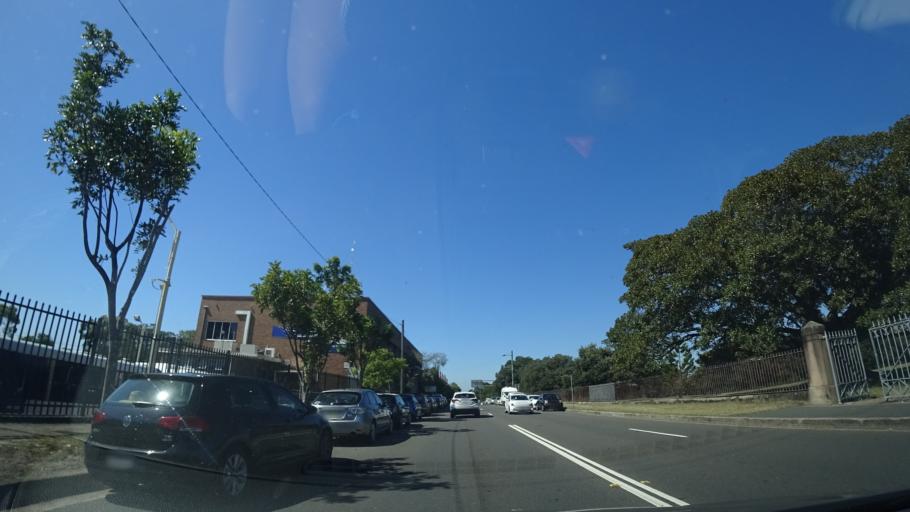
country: AU
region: New South Wales
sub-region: Waverley
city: Bondi Junction
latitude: -33.8905
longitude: 151.2420
